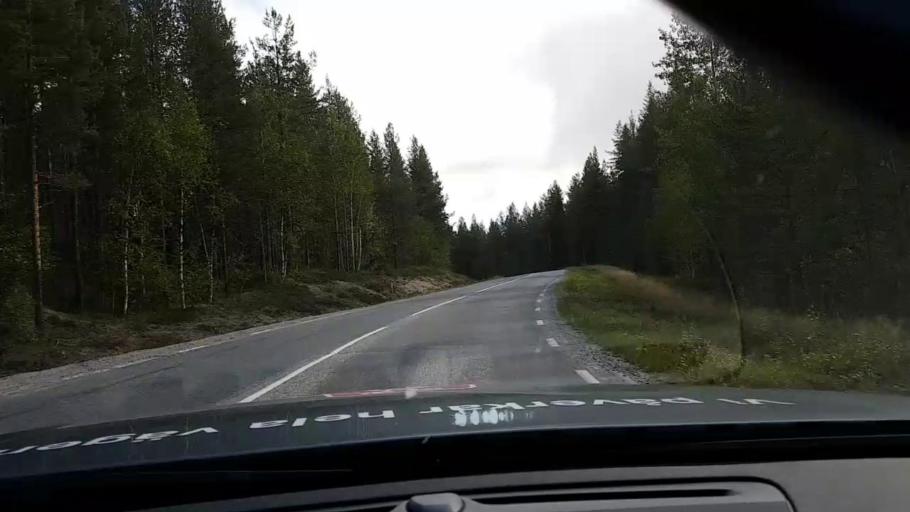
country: SE
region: Vaesterbotten
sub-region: Asele Kommun
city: Asele
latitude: 63.7943
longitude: 17.5763
